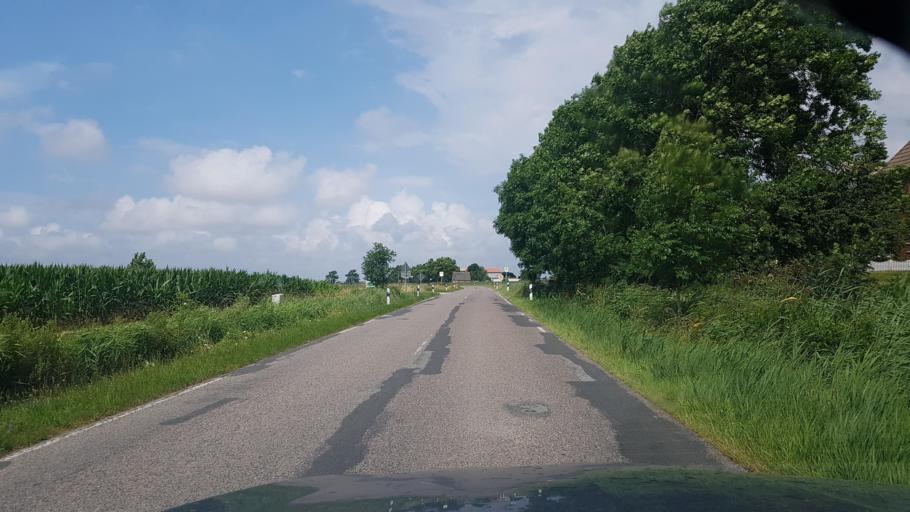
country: DE
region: Schleswig-Holstein
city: Elisabeth-Sophien-Koog
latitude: 54.4980
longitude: 8.8434
